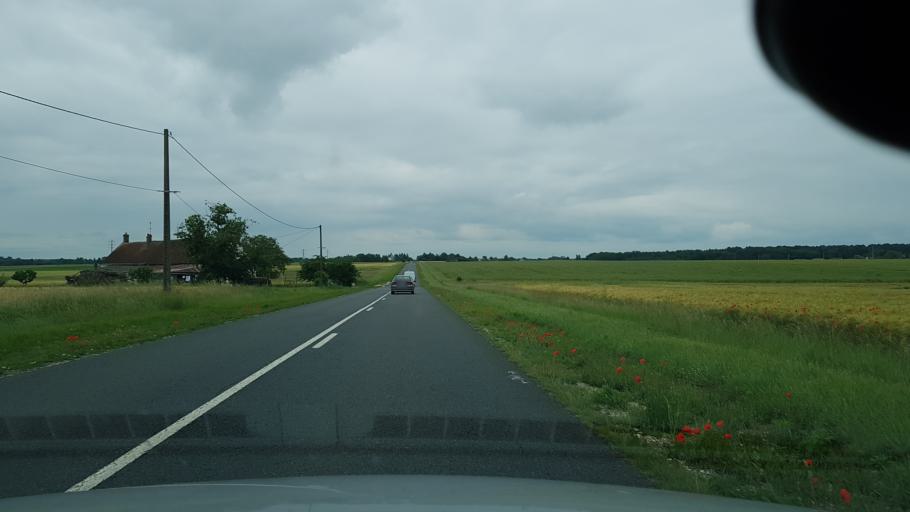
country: FR
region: Centre
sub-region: Departement du Loir-et-Cher
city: Chatillon-sur-Cher
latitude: 47.3004
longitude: 1.5131
